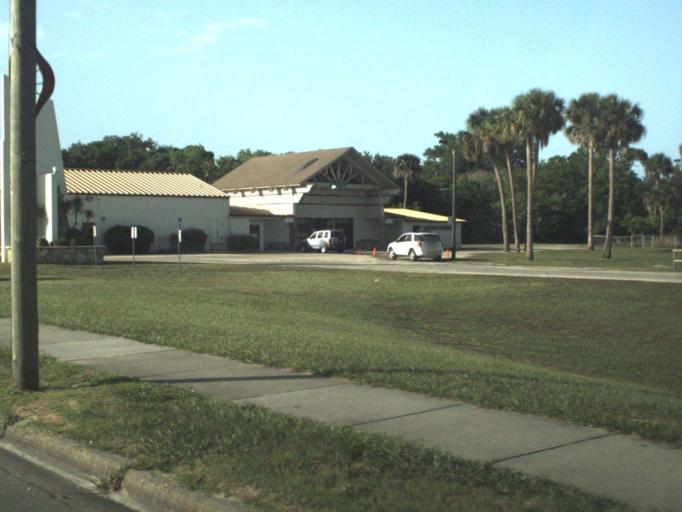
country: US
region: Florida
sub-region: Volusia County
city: Edgewater
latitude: 28.9938
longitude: -80.9088
